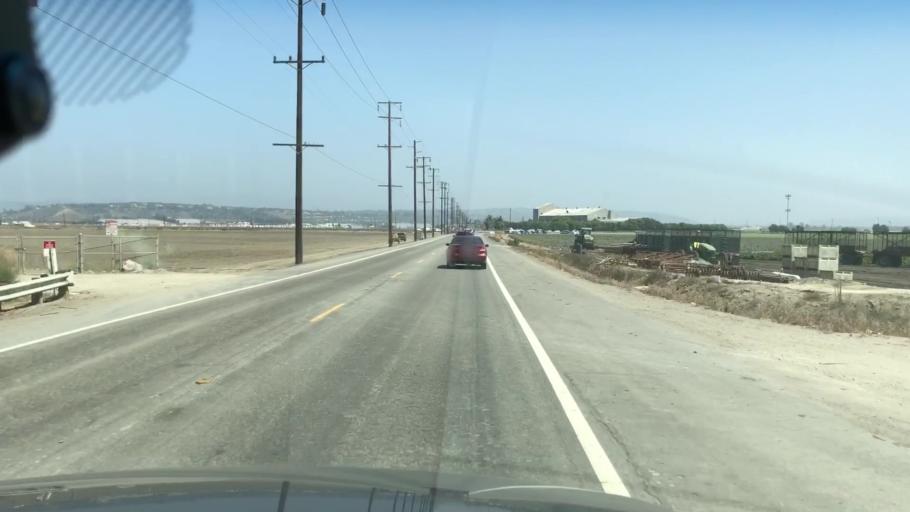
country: US
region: California
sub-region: Ventura County
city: Oxnard
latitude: 34.1929
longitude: -119.1079
